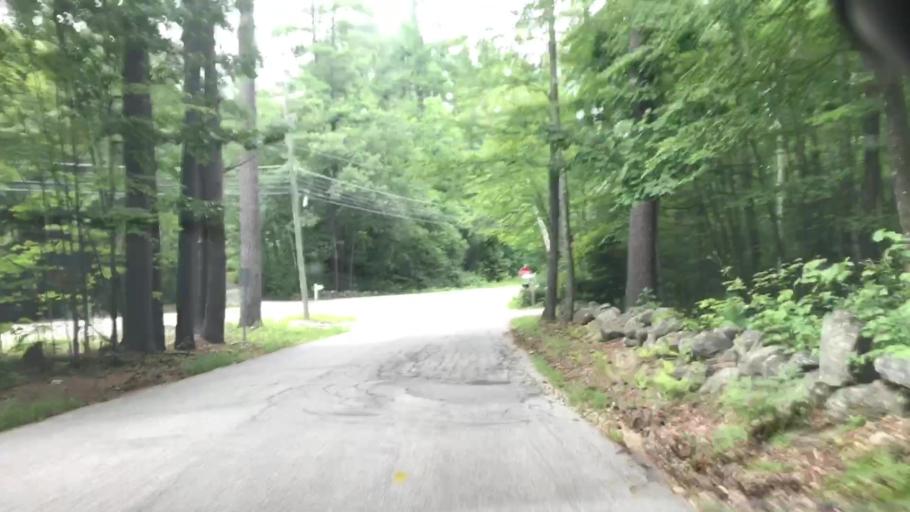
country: US
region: New Hampshire
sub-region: Hillsborough County
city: Milford
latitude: 42.8570
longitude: -71.6333
